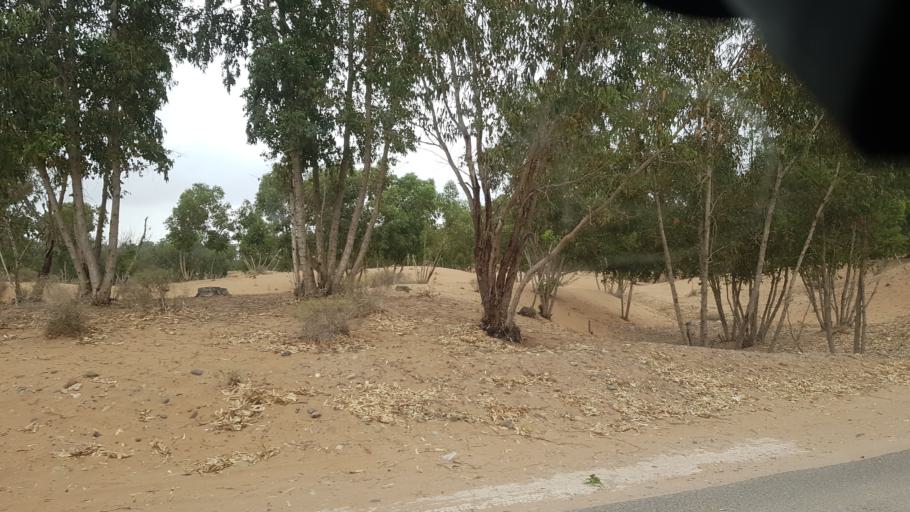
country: MA
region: Souss-Massa-Draa
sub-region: Inezgane-Ait Mellou
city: Inezgane
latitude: 30.3190
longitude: -9.5367
